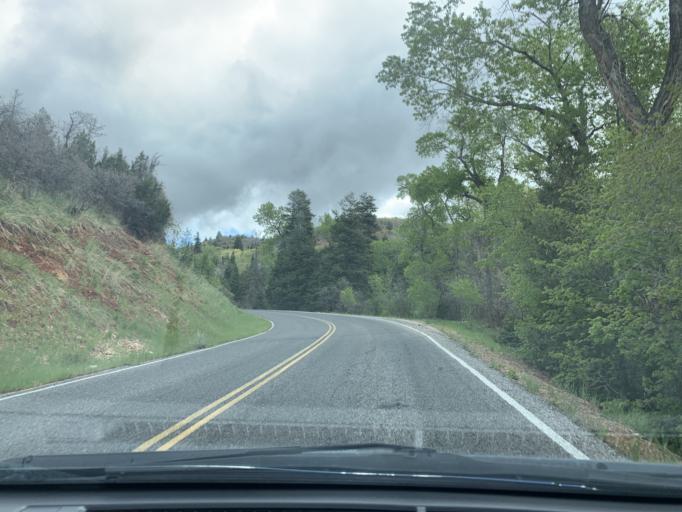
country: US
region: Utah
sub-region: Juab County
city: Nephi
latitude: 39.7799
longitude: -111.6934
